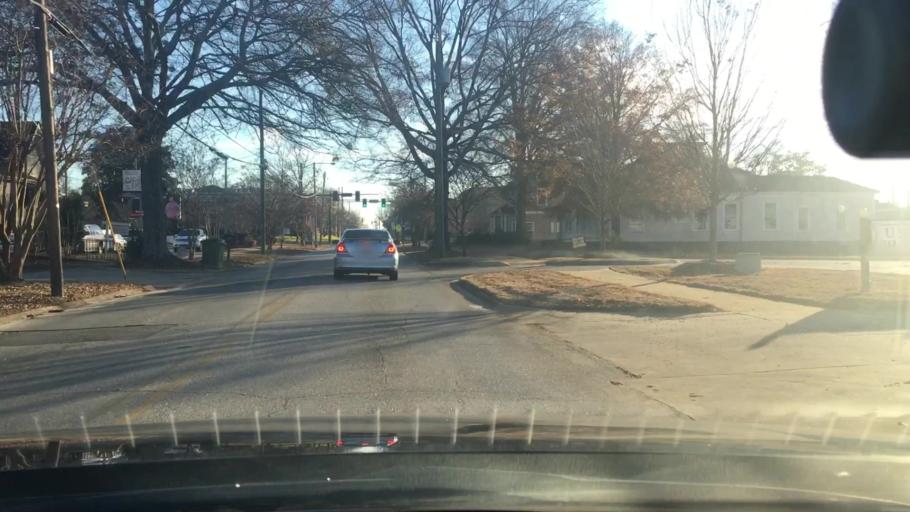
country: US
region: Georgia
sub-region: Spalding County
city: Griffin
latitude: 33.2458
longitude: -84.2669
